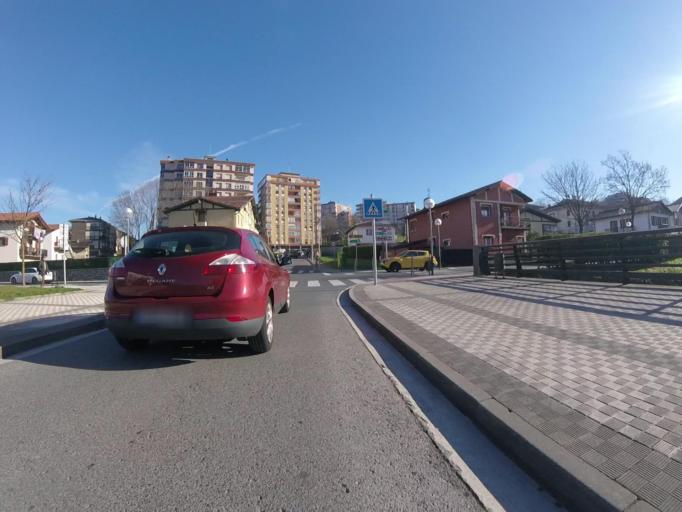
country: ES
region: Basque Country
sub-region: Provincia de Guipuzcoa
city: Irun
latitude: 43.3398
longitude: -1.7786
